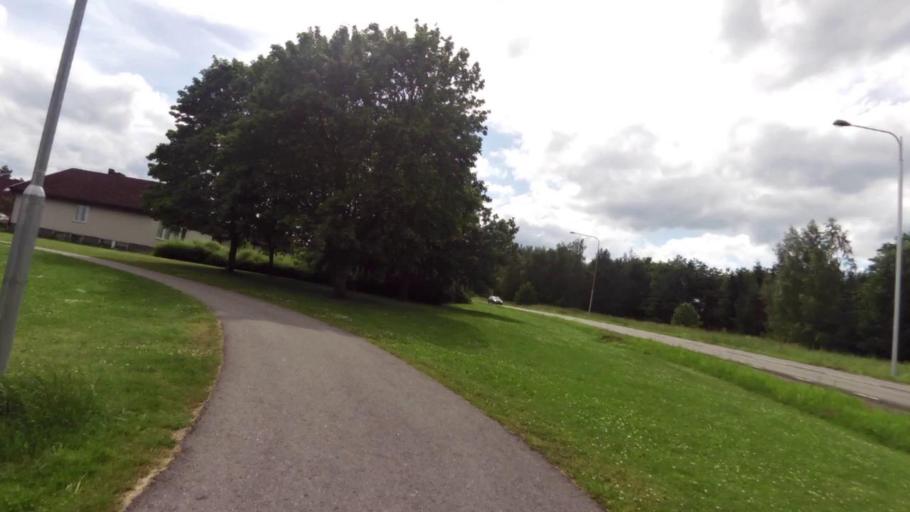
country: SE
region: OEstergoetland
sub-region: Linkopings Kommun
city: Malmslatt
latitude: 58.4179
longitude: 15.5563
